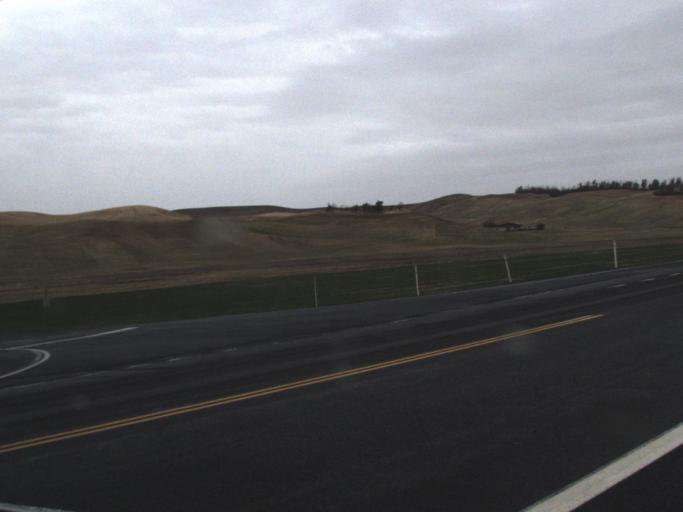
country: US
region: Washington
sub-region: Whitman County
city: Colfax
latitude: 46.7934
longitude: -117.3120
